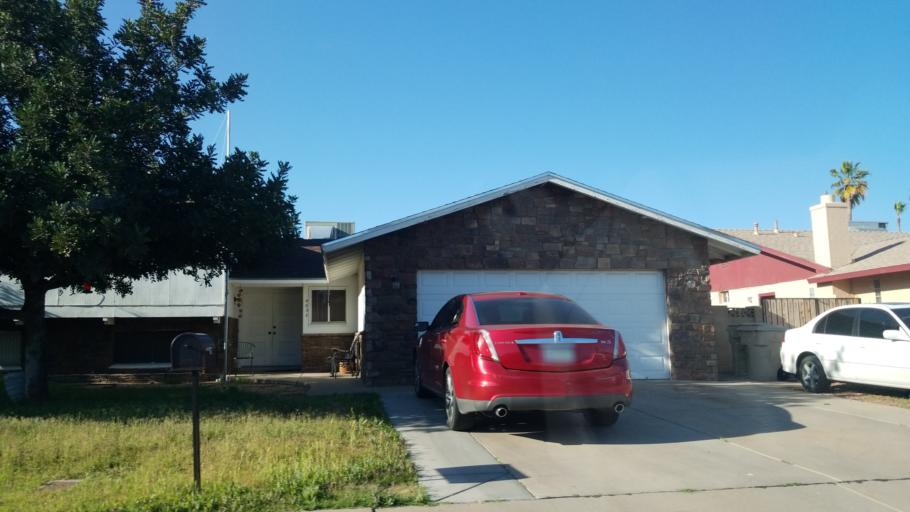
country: US
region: Arizona
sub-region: Maricopa County
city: Glendale
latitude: 33.5203
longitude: -112.1598
